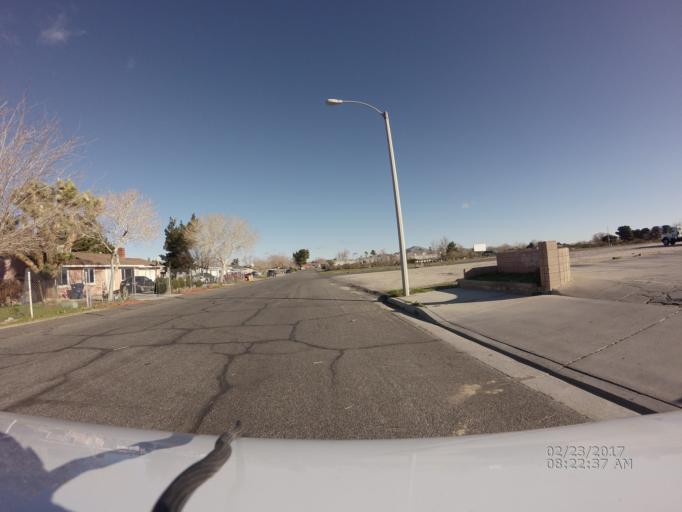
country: US
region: California
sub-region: Los Angeles County
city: Lake Los Angeles
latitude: 34.6121
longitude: -117.8279
